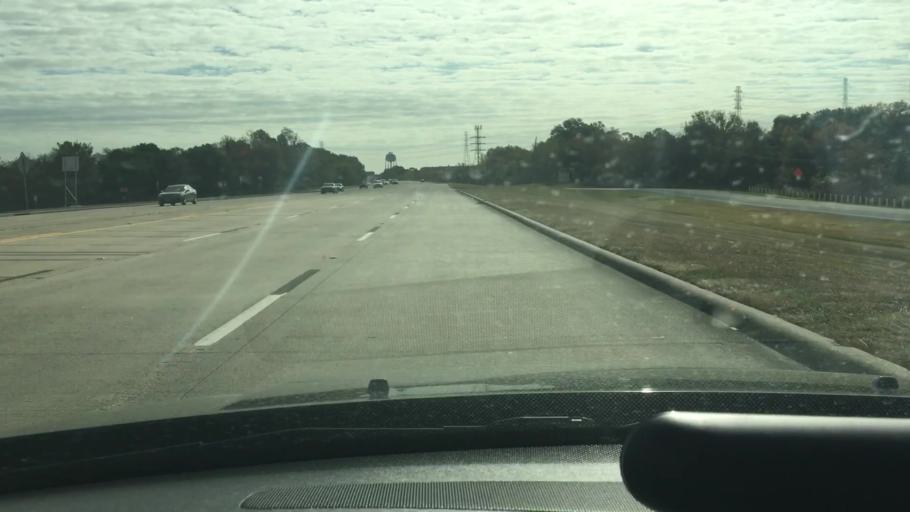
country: US
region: Texas
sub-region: Harris County
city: Nassau Bay
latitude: 29.5325
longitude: -95.0938
